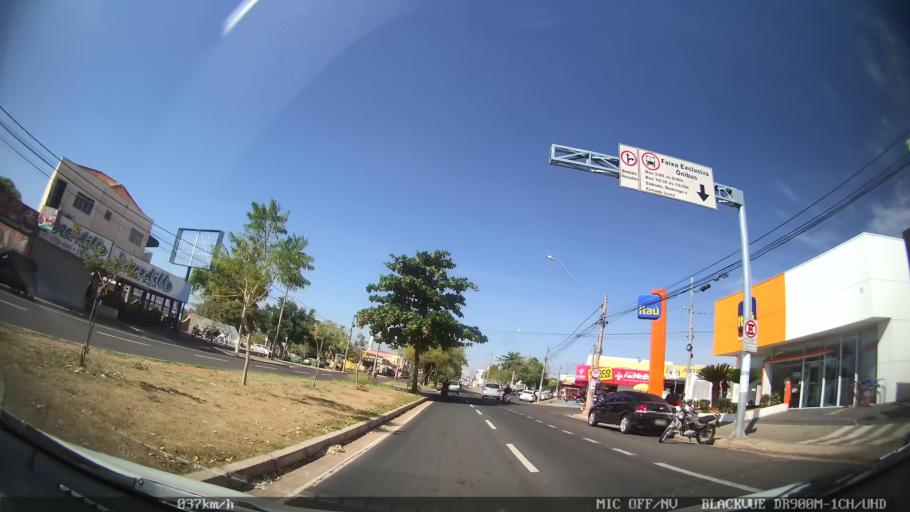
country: BR
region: Sao Paulo
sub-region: Sao Jose Do Rio Preto
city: Sao Jose do Rio Preto
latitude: -20.7812
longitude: -49.3997
